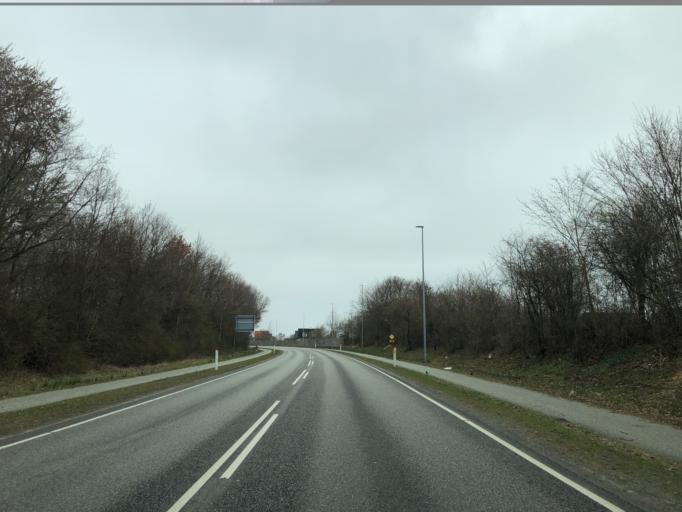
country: DK
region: North Denmark
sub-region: Frederikshavn Kommune
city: Frederikshavn
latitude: 57.4497
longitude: 10.5377
